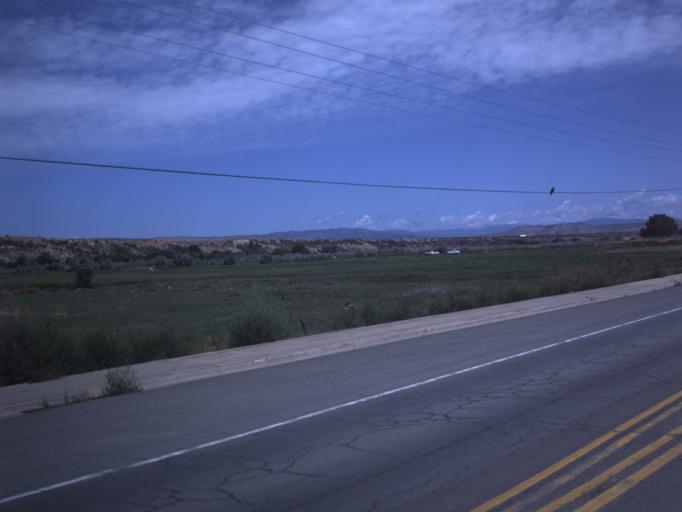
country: US
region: Utah
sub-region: Duchesne County
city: Duchesne
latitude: 40.1697
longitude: -110.4013
